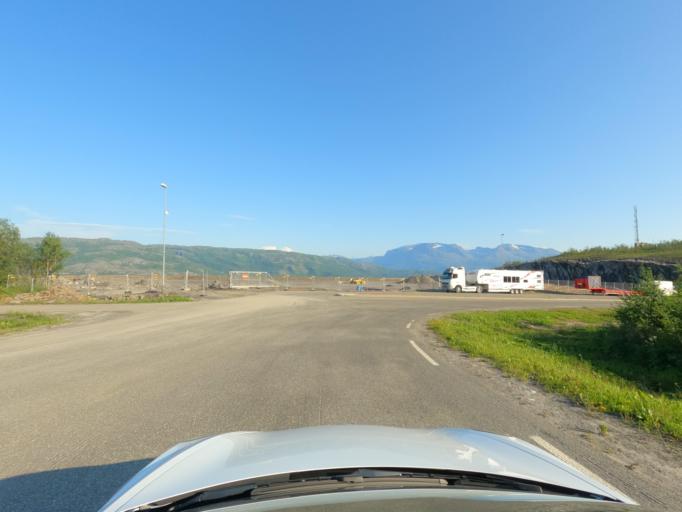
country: NO
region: Nordland
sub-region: Narvik
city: Bjerkvik
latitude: 68.5435
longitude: 17.4961
